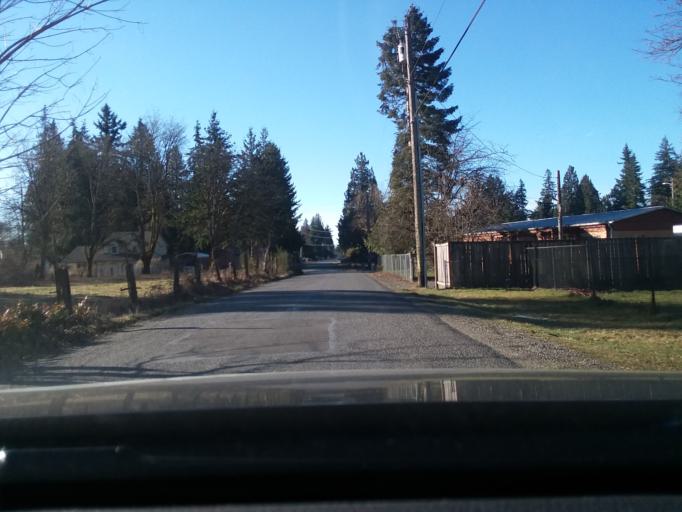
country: US
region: Washington
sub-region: Pierce County
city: Summit
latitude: 47.1334
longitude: -122.3628
